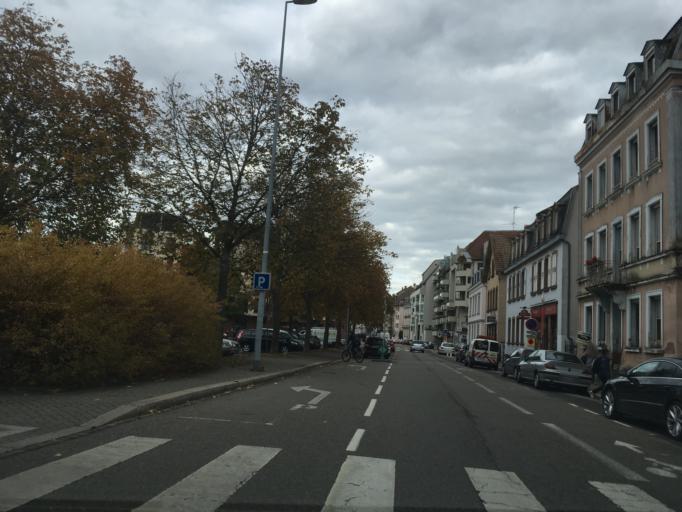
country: FR
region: Alsace
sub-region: Departement du Bas-Rhin
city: Strasbourg
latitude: 48.5679
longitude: 7.7519
